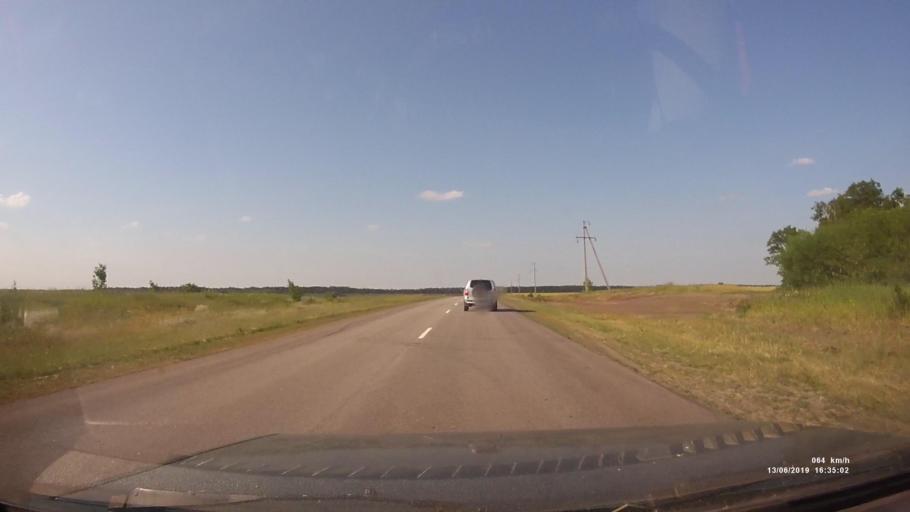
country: RU
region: Rostov
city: Kazanskaya
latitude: 49.8786
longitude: 41.2962
